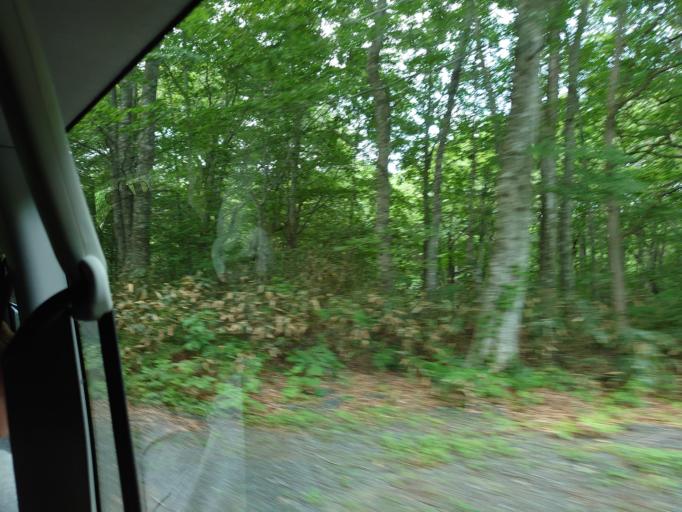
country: JP
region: Iwate
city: Ichinoseki
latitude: 38.9468
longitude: 140.8615
